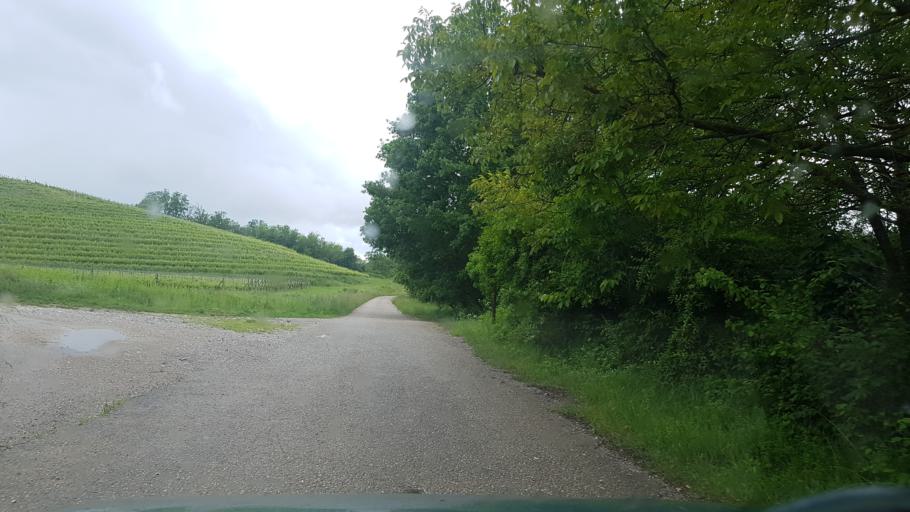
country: IT
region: Friuli Venezia Giulia
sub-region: Provincia di Gorizia
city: Mossa
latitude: 45.9444
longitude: 13.5800
